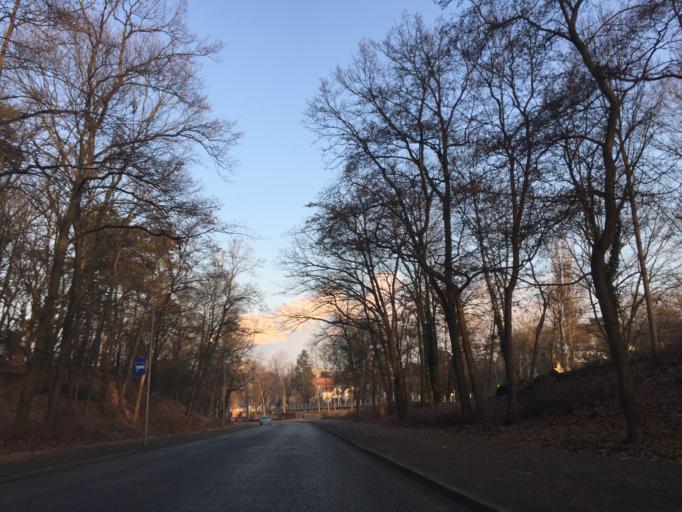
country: DE
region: Berlin
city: Haselhorst
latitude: 52.5207
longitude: 13.2464
